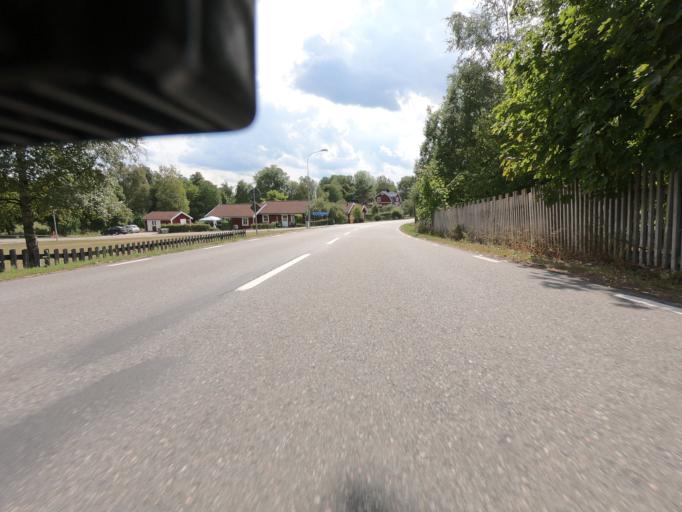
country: SE
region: Joenkoeping
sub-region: Vetlanda Kommun
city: Landsbro
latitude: 57.2696
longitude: 14.9229
